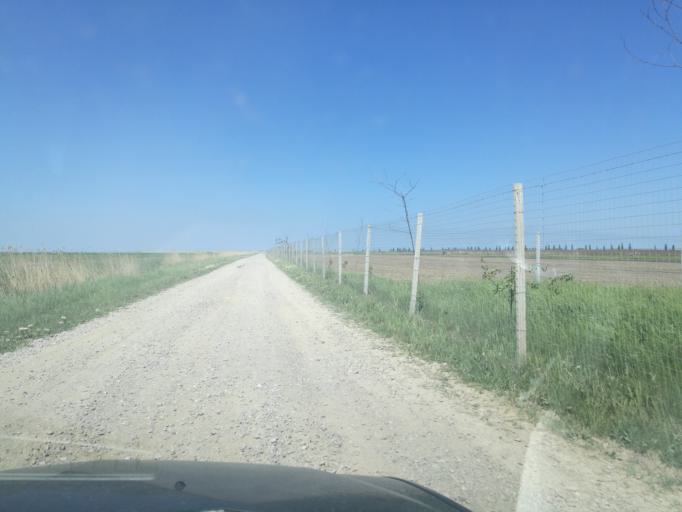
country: RO
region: Prahova
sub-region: Comuna Salciile
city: Salciile
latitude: 44.7800
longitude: 26.4700
